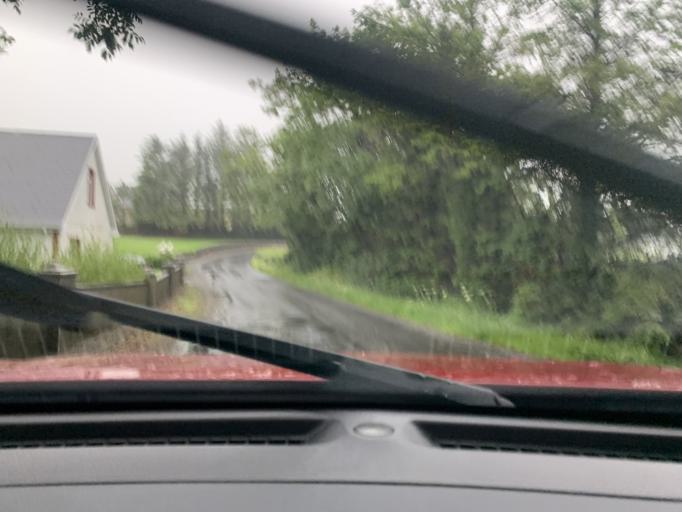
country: IE
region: Connaught
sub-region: Sligo
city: Sligo
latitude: 54.3285
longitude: -8.4209
